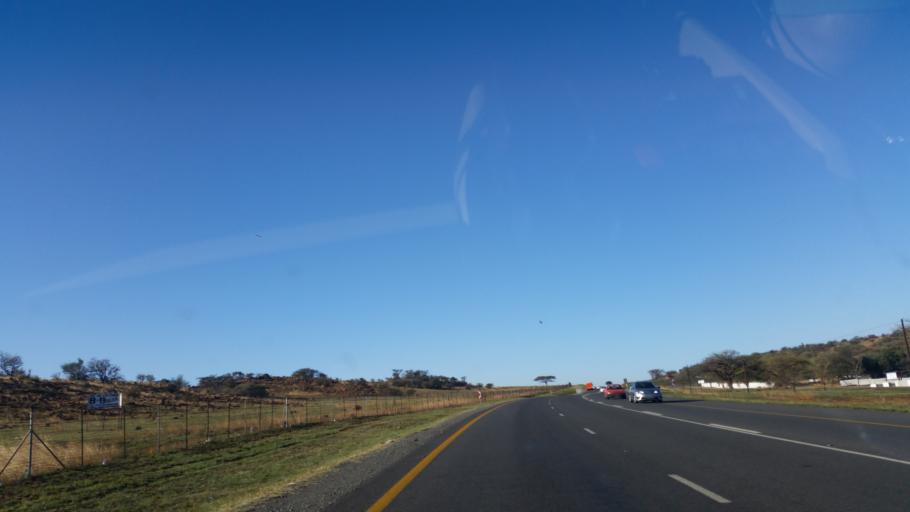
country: ZA
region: KwaZulu-Natal
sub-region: Amajuba District Municipality
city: Newcastle
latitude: -27.8010
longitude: 29.9566
